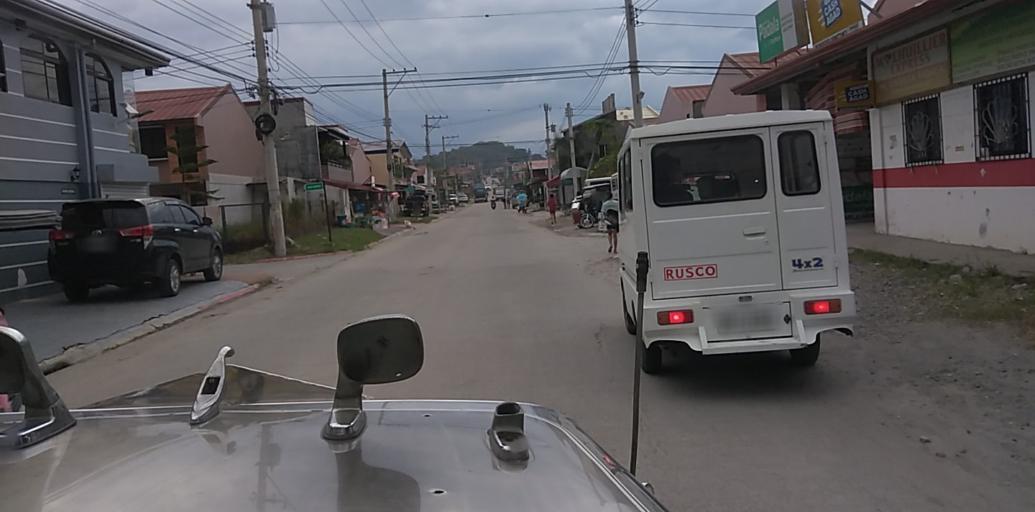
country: PH
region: Central Luzon
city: Santol
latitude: 15.1665
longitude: 120.5323
